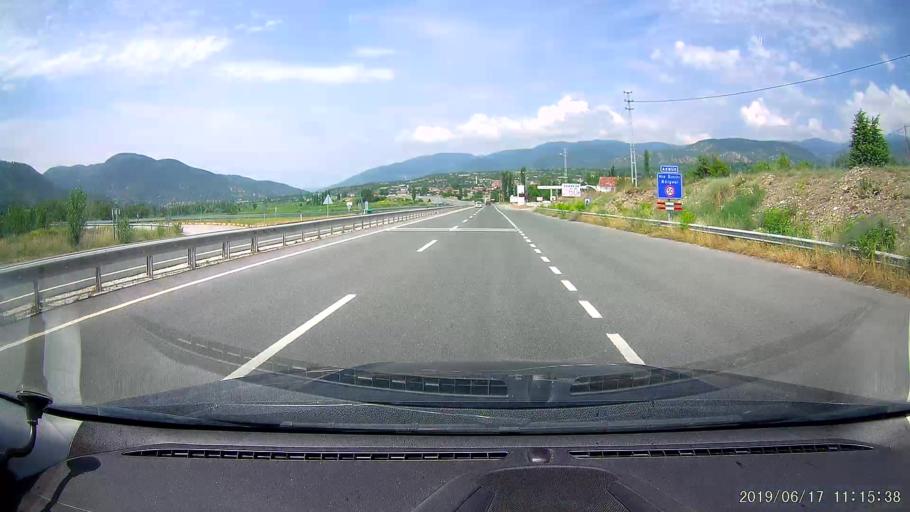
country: TR
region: Kastamonu
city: Tosya
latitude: 40.9509
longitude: 33.9194
